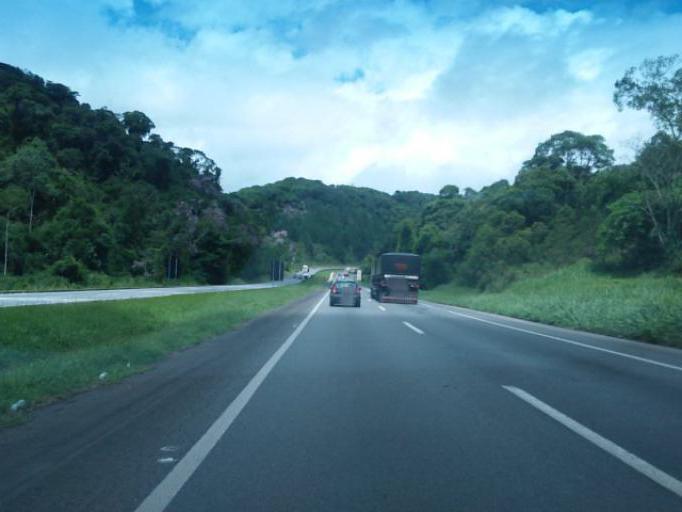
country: BR
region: Parana
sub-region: Antonina
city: Antonina
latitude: -25.0824
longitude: -48.6170
